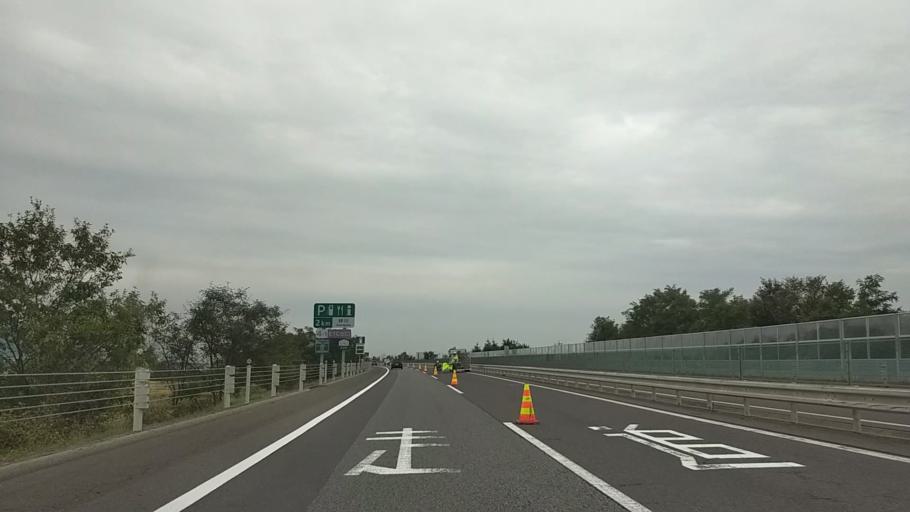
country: JP
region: Nagano
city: Toyoshina
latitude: 36.2909
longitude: 137.9279
